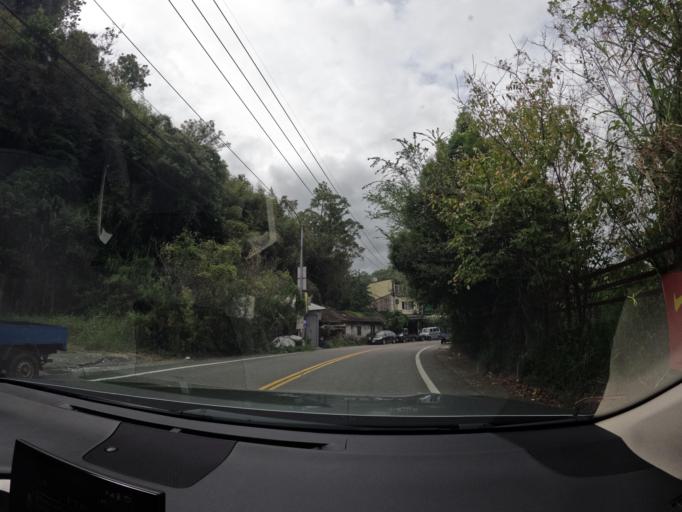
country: TW
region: Taiwan
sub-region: Miaoli
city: Miaoli
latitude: 24.3968
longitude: 120.8664
